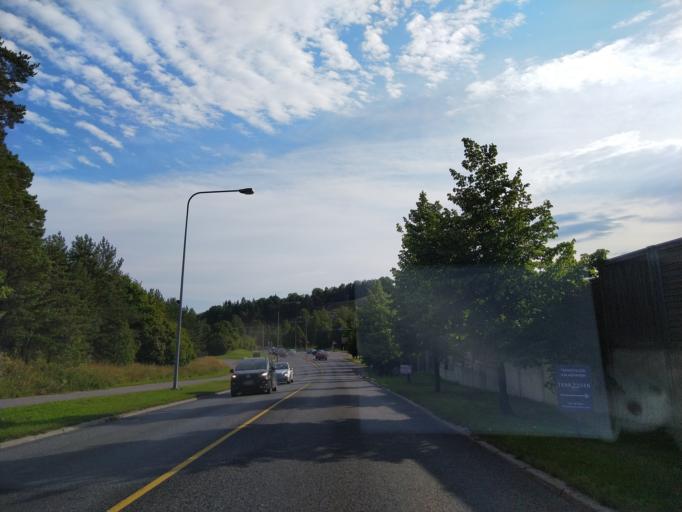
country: FI
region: Varsinais-Suomi
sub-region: Turku
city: Turku
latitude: 60.4192
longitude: 22.2316
